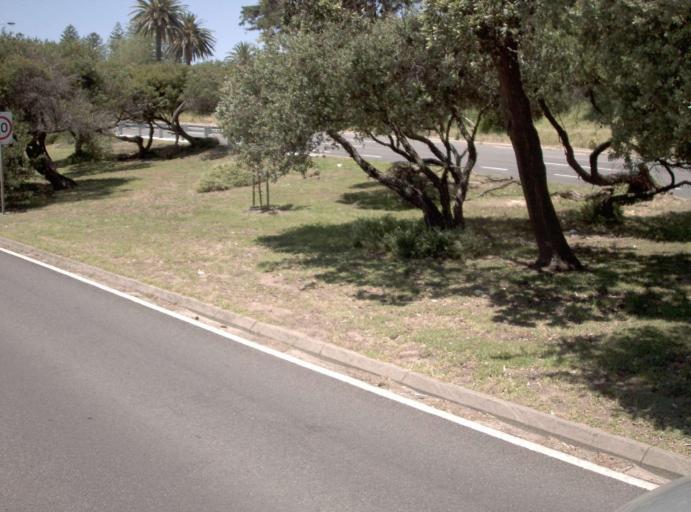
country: AU
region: Victoria
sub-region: Frankston
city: Frankston
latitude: -38.1468
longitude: 145.1183
